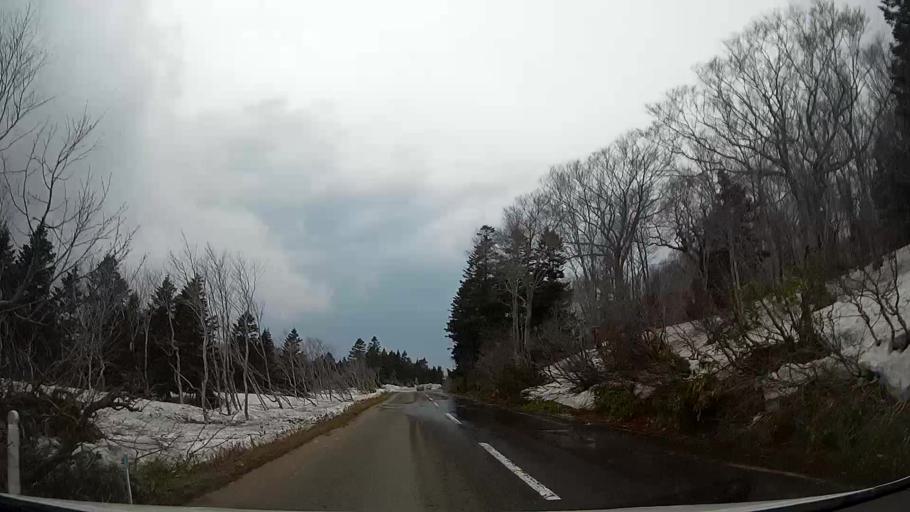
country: JP
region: Aomori
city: Aomori Shi
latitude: 40.6364
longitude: 140.8694
